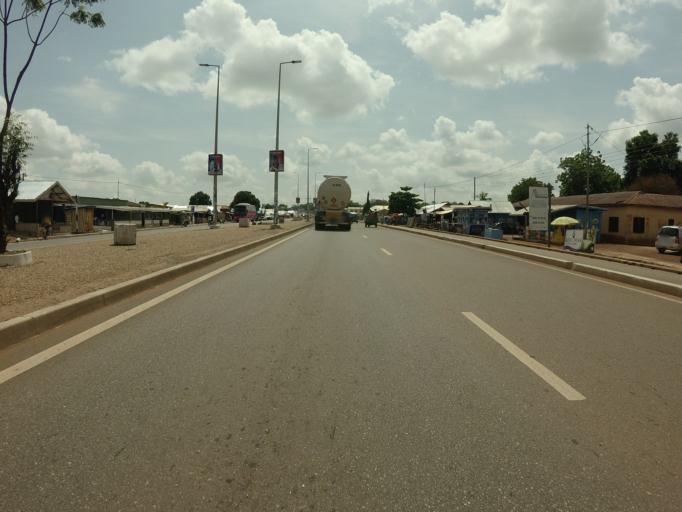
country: GH
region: Northern
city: Tamale
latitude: 9.3979
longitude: -0.8292
